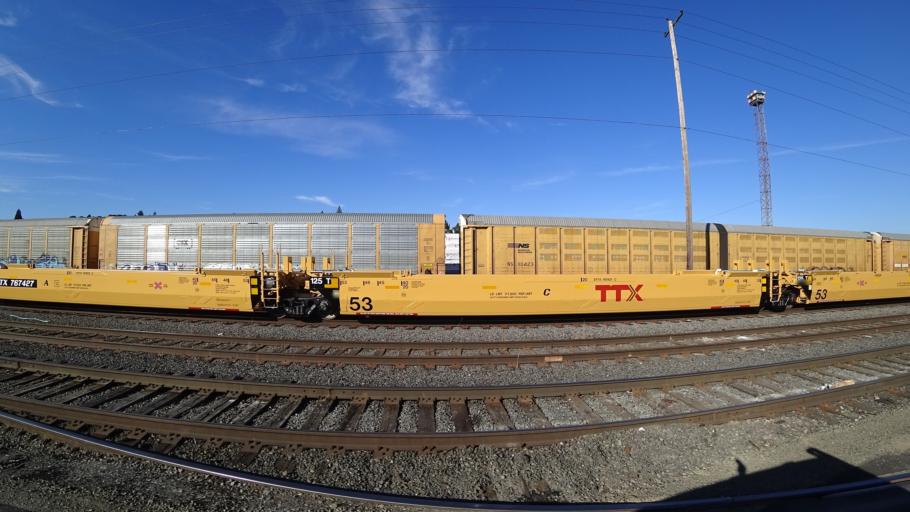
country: US
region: Oregon
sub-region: Multnomah County
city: Portland
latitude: 45.5463
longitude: -122.6899
